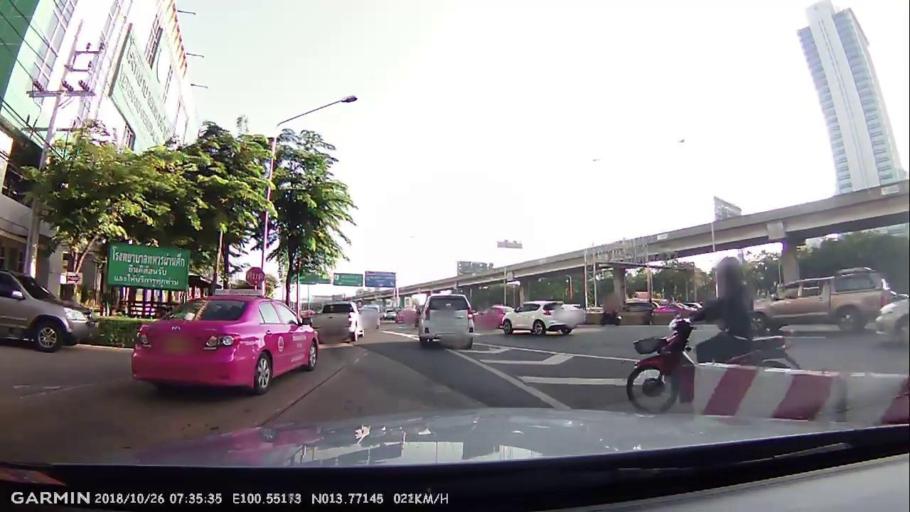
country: TH
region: Bangkok
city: Din Daeng
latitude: 13.7715
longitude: 100.5517
